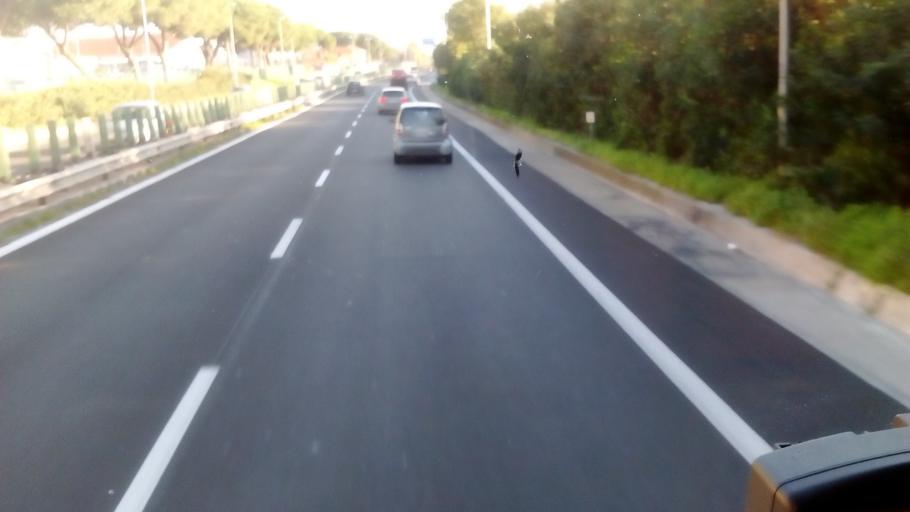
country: IT
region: Latium
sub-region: Citta metropolitana di Roma Capitale
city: Ciampino
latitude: 41.7914
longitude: 12.5932
